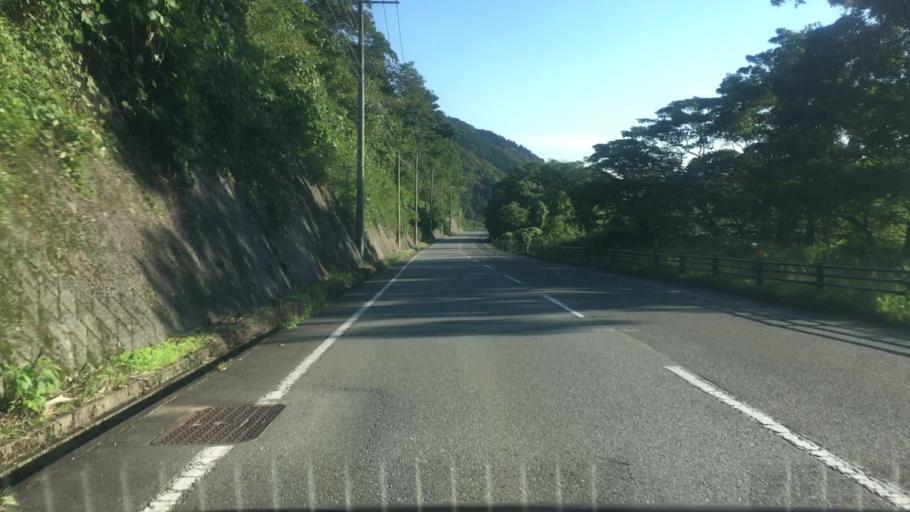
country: JP
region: Hyogo
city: Toyooka
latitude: 35.6017
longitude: 134.8060
